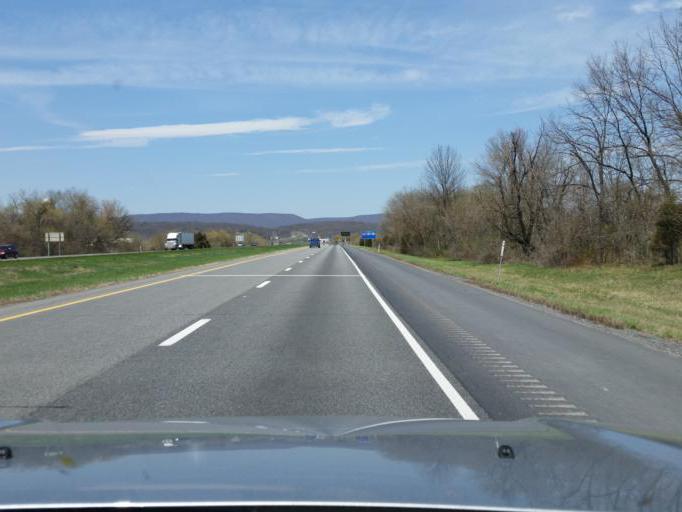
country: US
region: Pennsylvania
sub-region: Juniata County
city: Mifflintown
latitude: 40.5674
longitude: -77.3659
